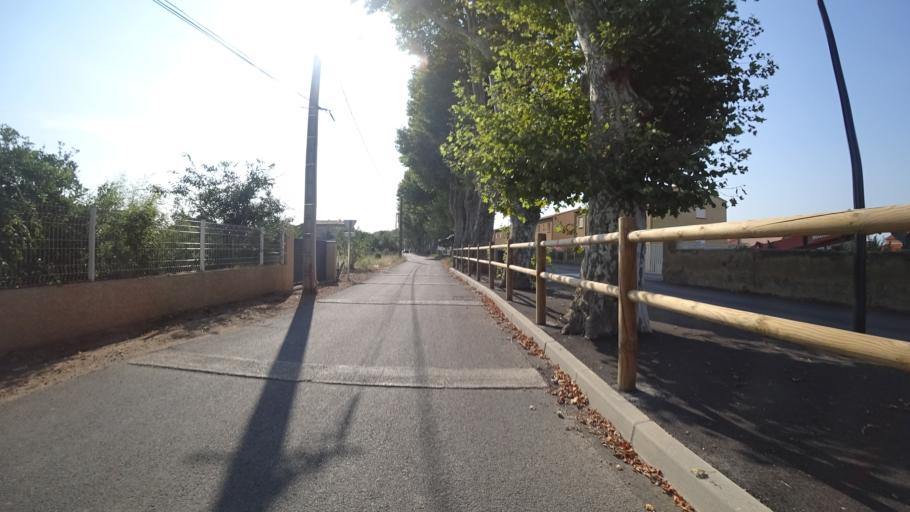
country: FR
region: Languedoc-Roussillon
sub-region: Departement des Pyrenees-Orientales
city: Claira
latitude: 42.7603
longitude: 2.9593
